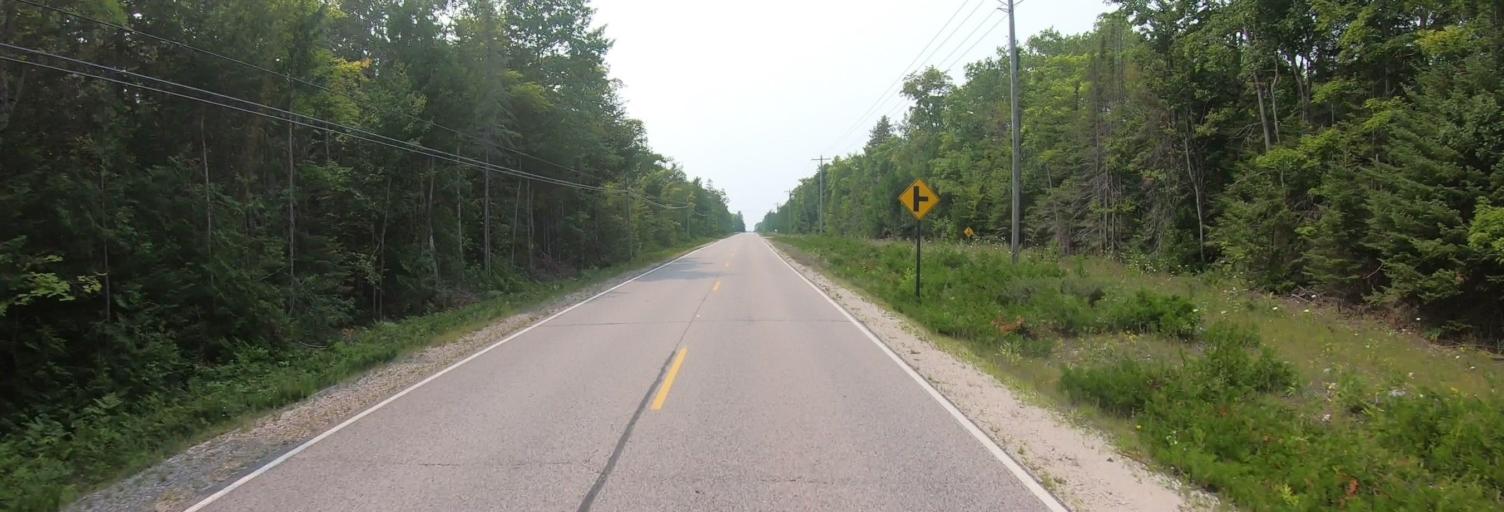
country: CA
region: Ontario
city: Thessalon
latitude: 46.0001
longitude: -83.9443
